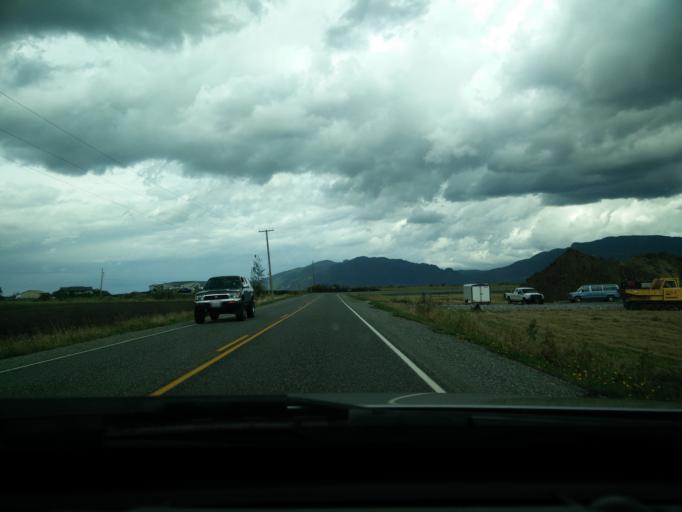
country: US
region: Washington
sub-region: Skagit County
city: Anacortes
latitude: 48.5524
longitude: -122.4663
